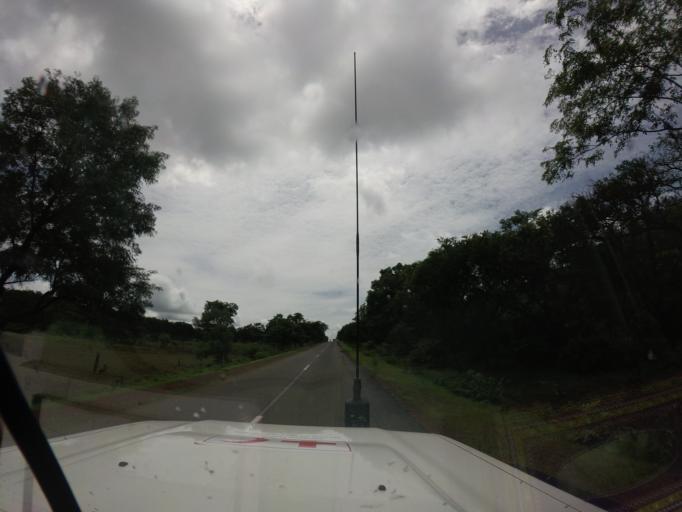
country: SL
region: Northern Province
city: Gberia Fotombu
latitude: 10.0379
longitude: -10.9937
